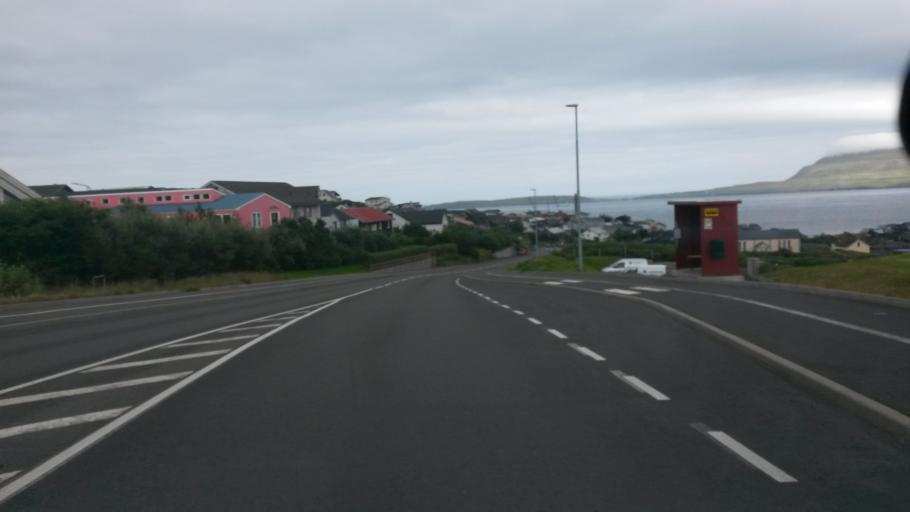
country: FO
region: Streymoy
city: Argir
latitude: 62.0006
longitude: -6.7956
